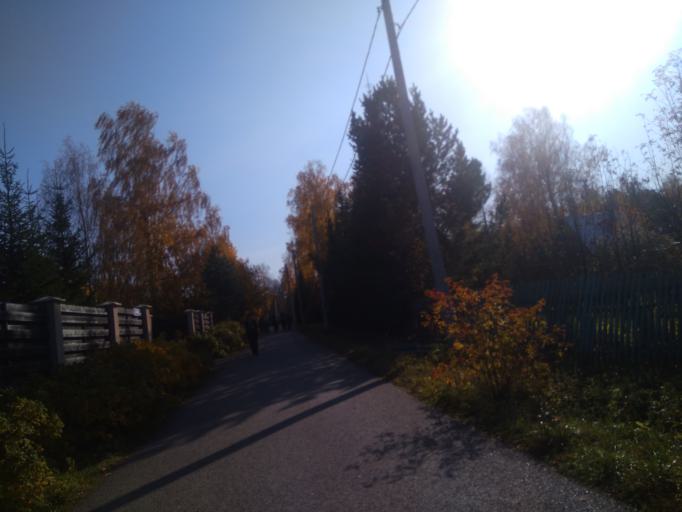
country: RU
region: Sverdlovsk
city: Mikhaylovsk
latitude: 56.5242
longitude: 59.2303
